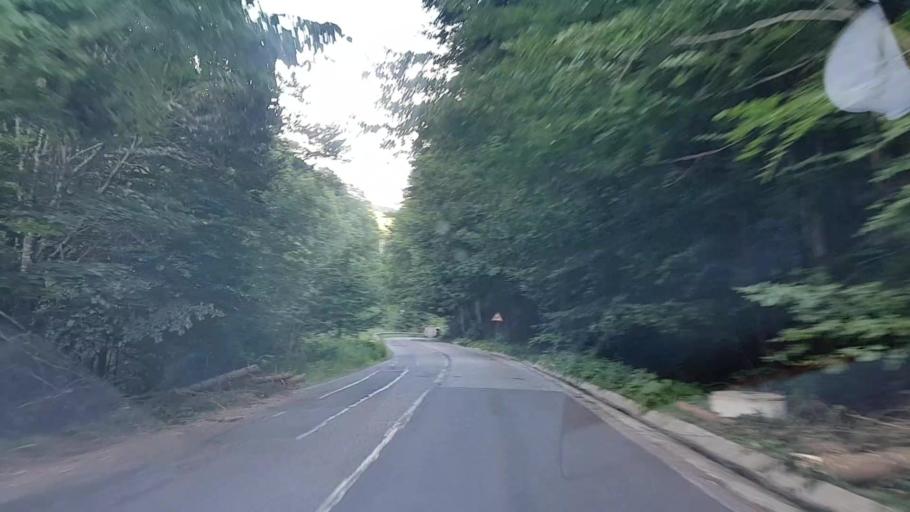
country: RO
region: Harghita
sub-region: Comuna Praid
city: Ocna de Sus
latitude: 46.5963
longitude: 25.2404
